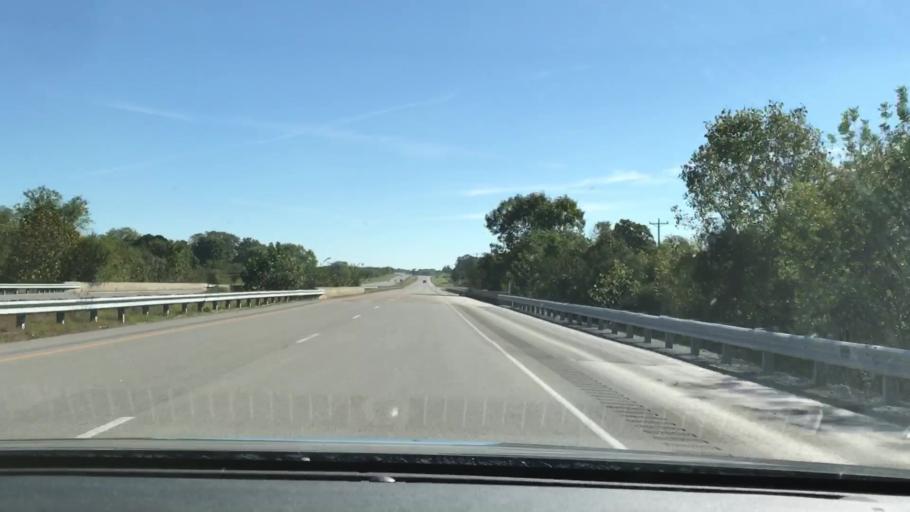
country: US
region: Kentucky
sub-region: Christian County
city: Hopkinsville
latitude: 36.8499
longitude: -87.3532
